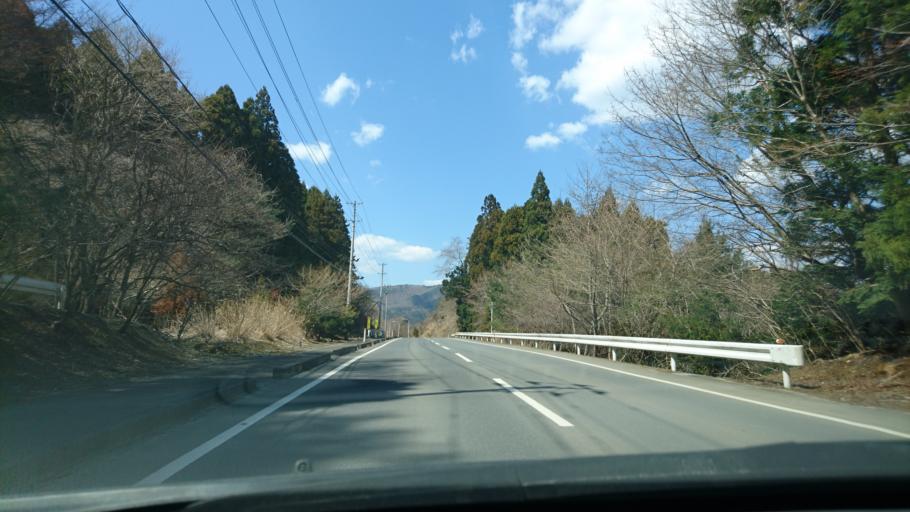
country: JP
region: Miyagi
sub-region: Oshika Gun
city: Onagawa Cho
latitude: 38.5079
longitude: 141.4857
